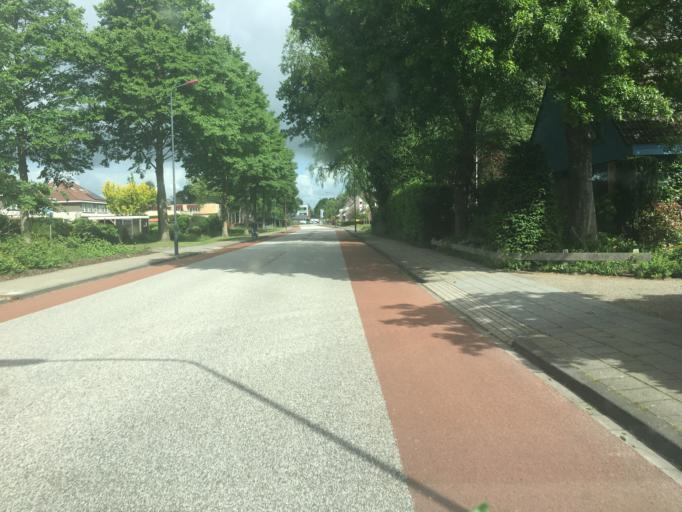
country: NL
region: Friesland
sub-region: Gemeente Heerenveen
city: Heerenveen
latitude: 52.9488
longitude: 5.9156
